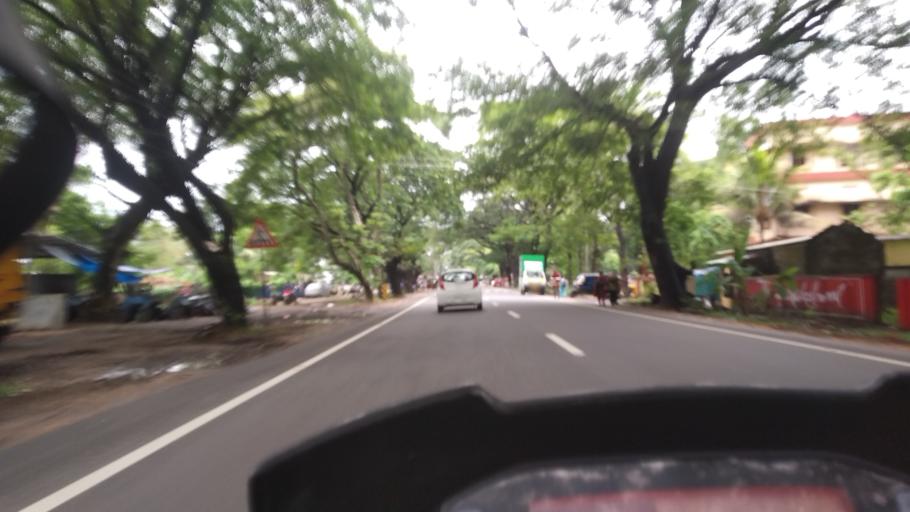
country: IN
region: Kerala
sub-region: Alappuzha
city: Alleppey
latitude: 9.4608
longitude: 76.3400
